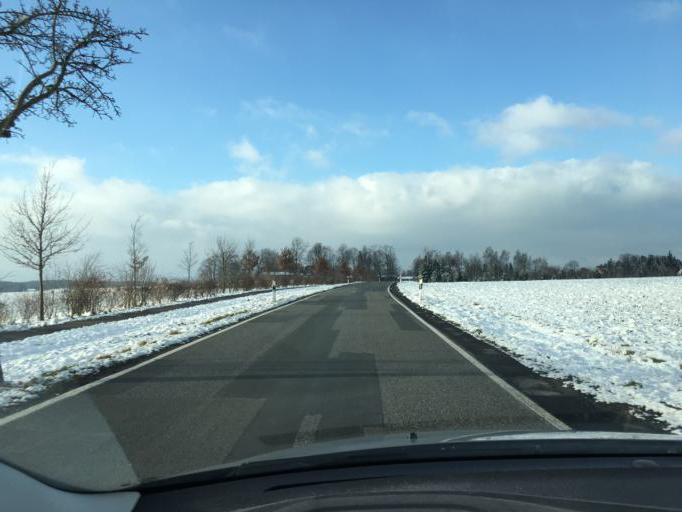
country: DE
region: Saxony
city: Grimma
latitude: 51.2540
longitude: 12.6966
